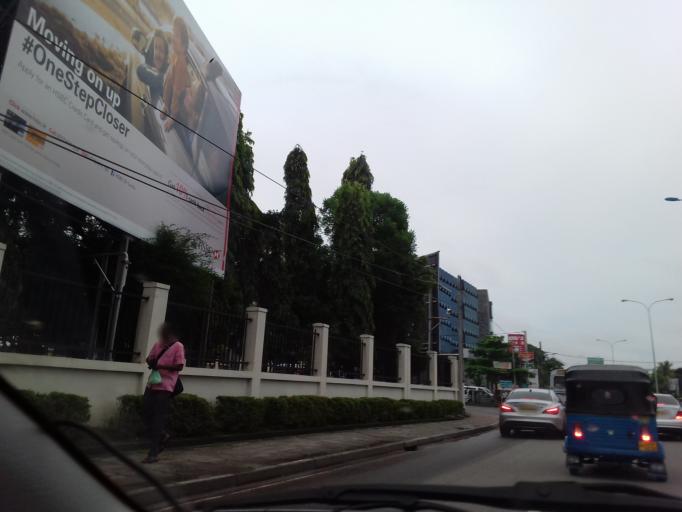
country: LK
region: Western
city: Pita Kotte
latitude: 6.9070
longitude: 79.9011
